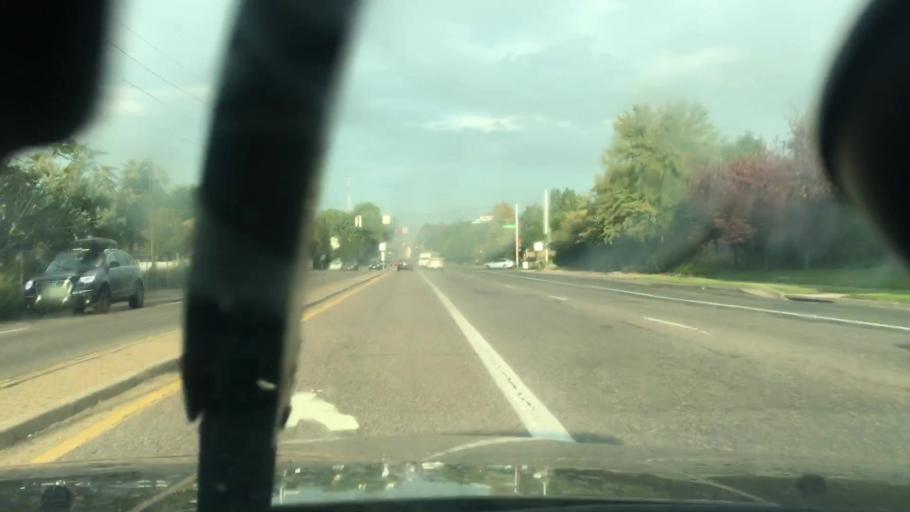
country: US
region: Colorado
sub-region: Arapahoe County
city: Glendale
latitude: 39.6746
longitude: -104.8858
